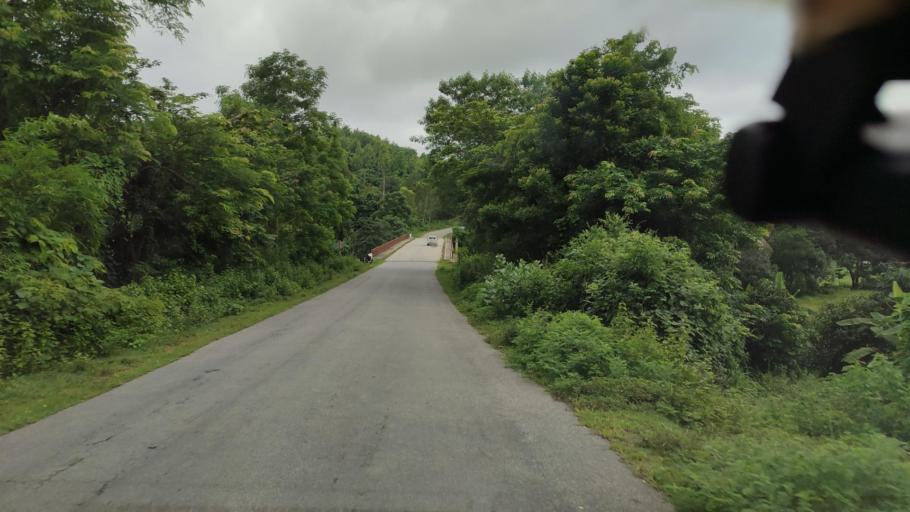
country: MM
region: Mandalay
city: Nay Pyi Taw
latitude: 19.9952
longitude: 95.9125
